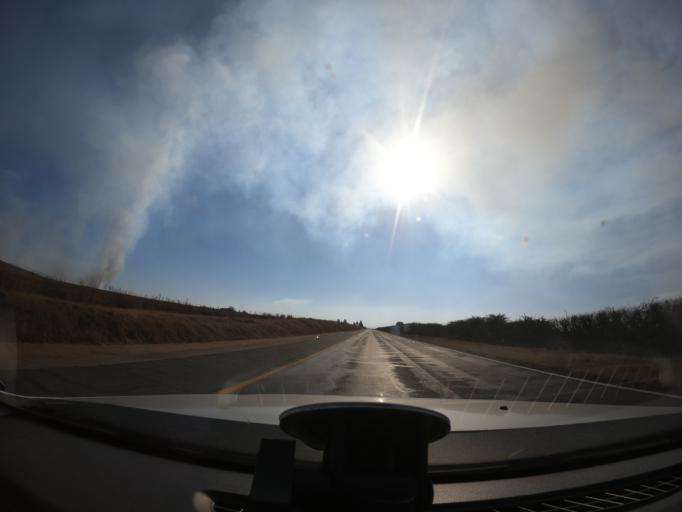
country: ZA
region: Gauteng
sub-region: Sedibeng District Municipality
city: Heidelberg
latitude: -26.4553
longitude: 28.3243
